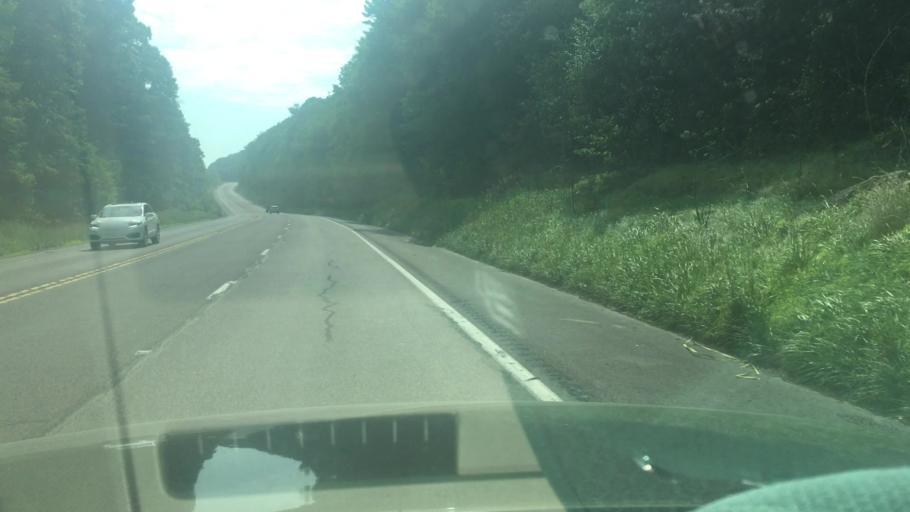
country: US
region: Pennsylvania
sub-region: Northumberland County
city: Kulpmont
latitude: 40.8205
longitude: -76.4875
